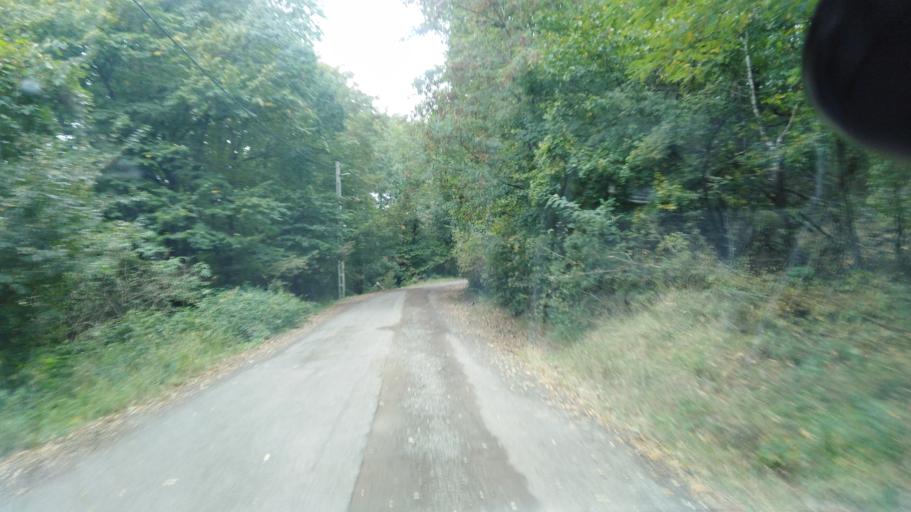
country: HU
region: Nograd
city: Somoskoujfalu
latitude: 48.1438
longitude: 19.8658
